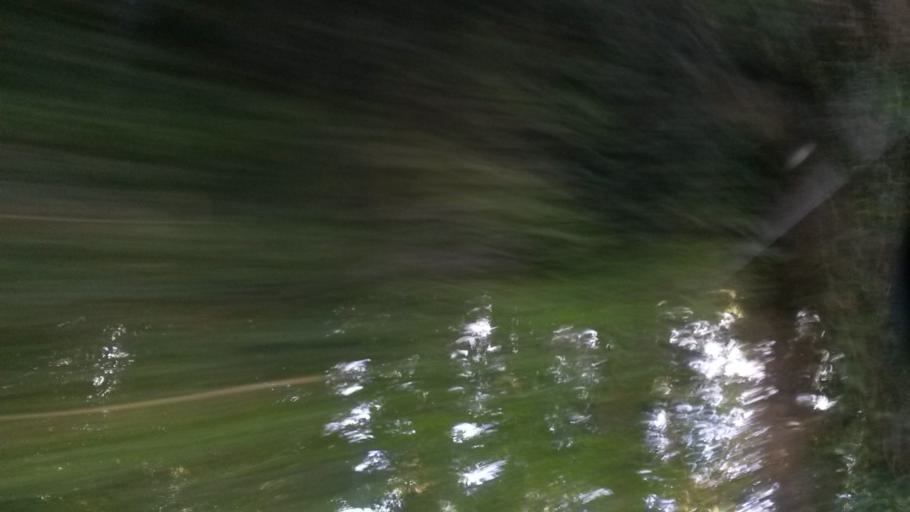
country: IE
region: Leinster
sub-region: An Mhi
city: Ashbourne
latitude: 53.5506
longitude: -6.3759
